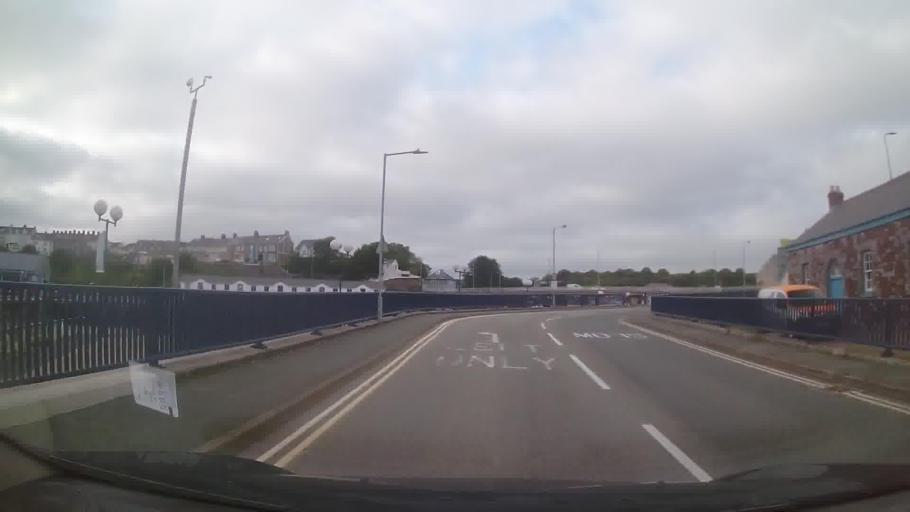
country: GB
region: Wales
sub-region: Pembrokeshire
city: Milford Haven
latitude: 51.7130
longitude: -5.0406
